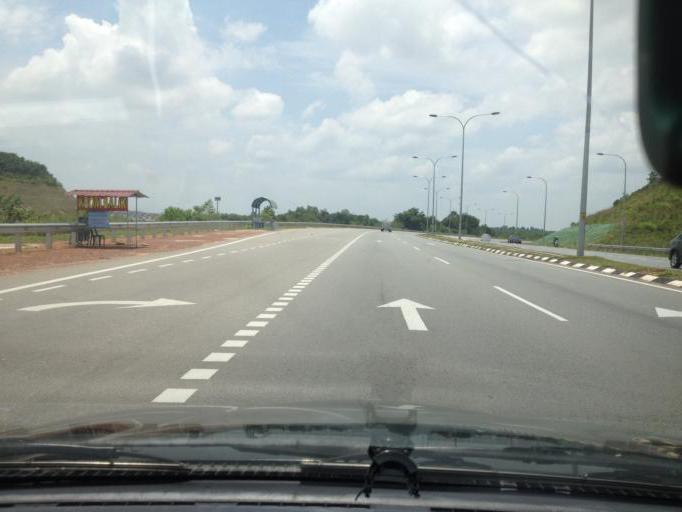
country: MY
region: Kedah
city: Sungai Petani
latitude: 5.6114
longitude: 100.5678
